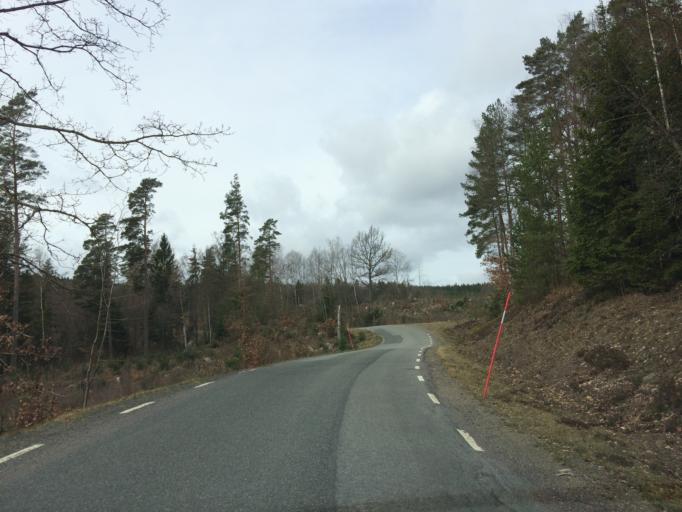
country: SE
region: Skane
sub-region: Ostra Goinge Kommun
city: Sibbhult
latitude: 56.2832
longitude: 14.2919
